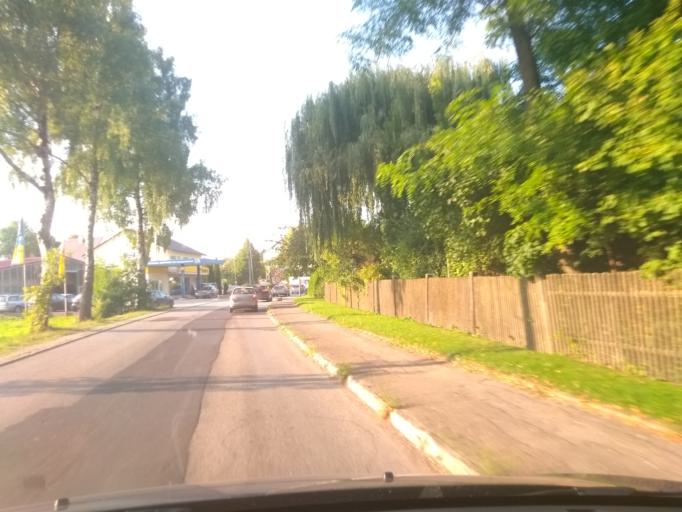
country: DE
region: Bavaria
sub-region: Upper Bavaria
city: Schwabhausen
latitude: 48.3195
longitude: 11.3864
